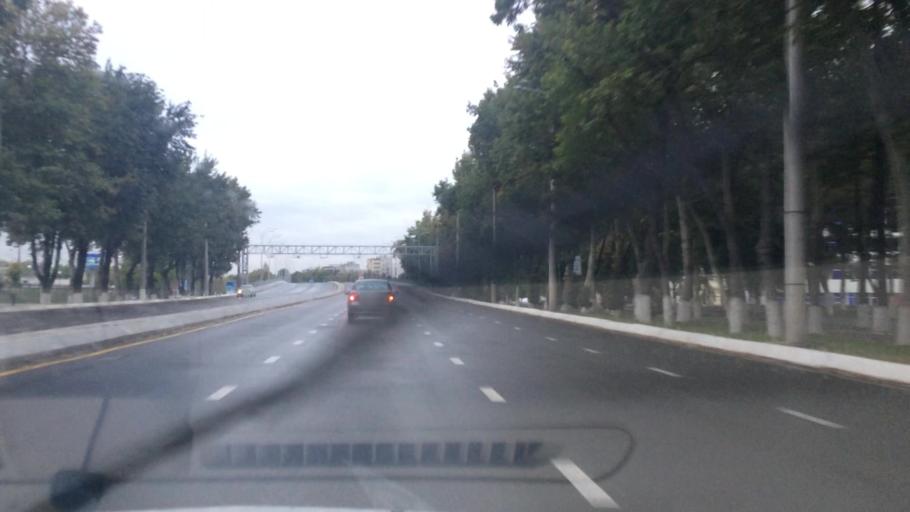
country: UZ
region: Toshkent Shahri
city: Tashkent
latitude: 41.2769
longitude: 69.2067
